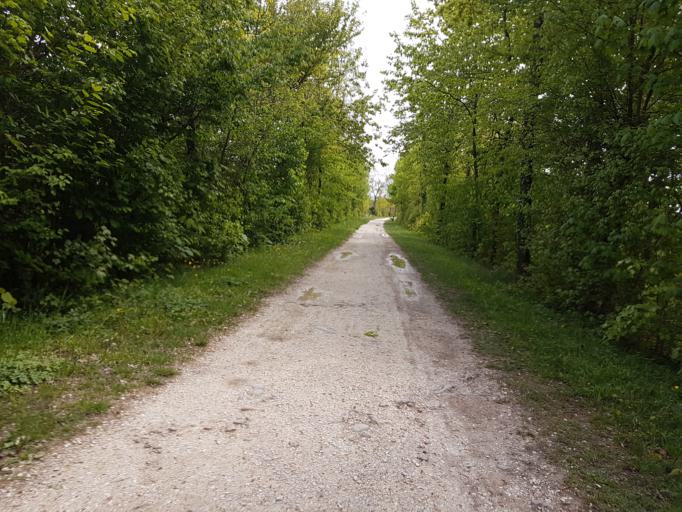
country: CH
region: Aargau
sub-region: Bezirk Brugg
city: Veltheim
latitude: 47.4288
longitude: 8.1609
